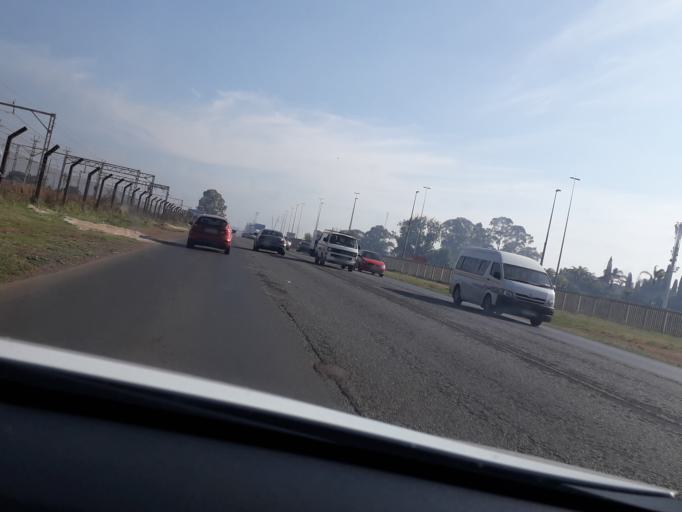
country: ZA
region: Gauteng
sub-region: City of Johannesburg Metropolitan Municipality
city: Modderfontein
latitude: -26.1447
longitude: 28.2189
